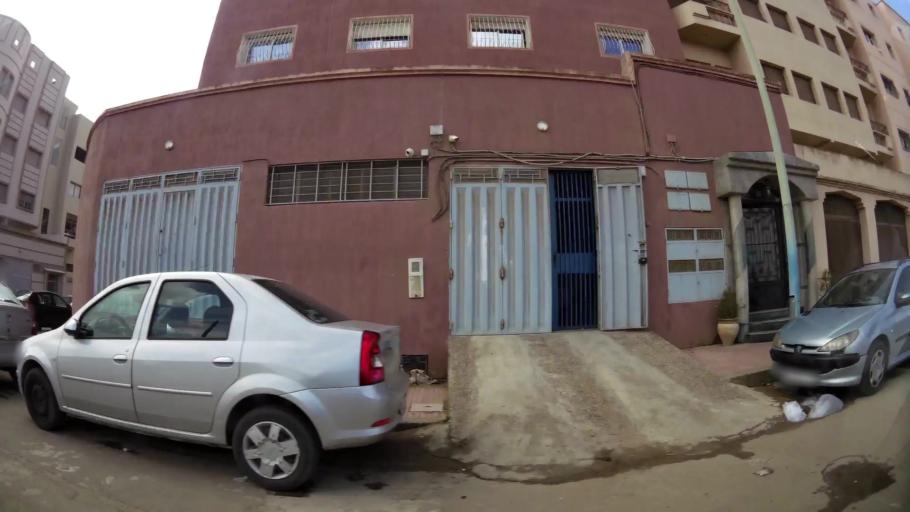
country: MA
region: Grand Casablanca
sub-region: Casablanca
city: Casablanca
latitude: 33.5296
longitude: -7.6005
